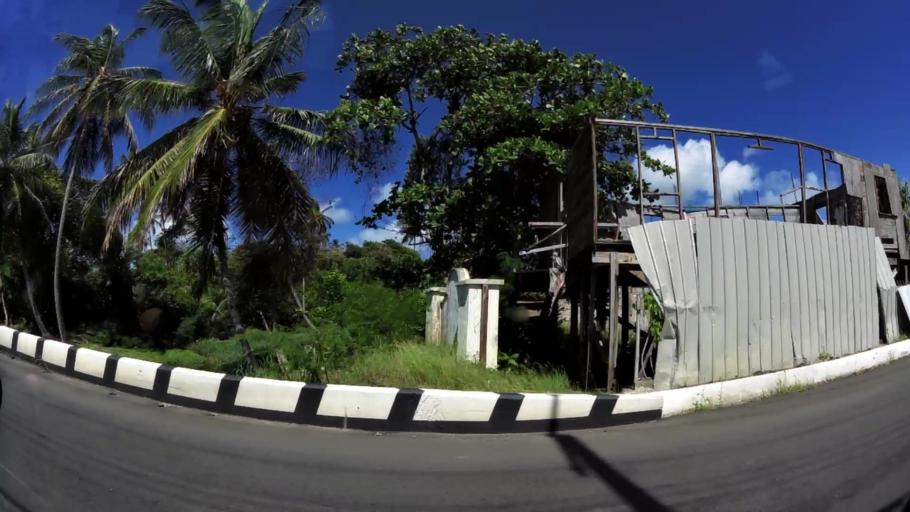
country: TT
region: Tobago
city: Scarborough
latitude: 11.1653
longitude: -60.7643
